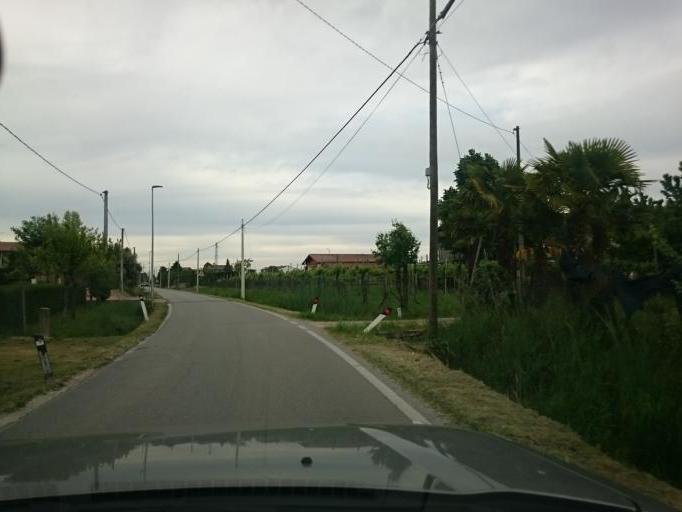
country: IT
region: Veneto
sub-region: Provincia di Padova
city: Bertipaglia
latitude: 45.3004
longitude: 11.8752
